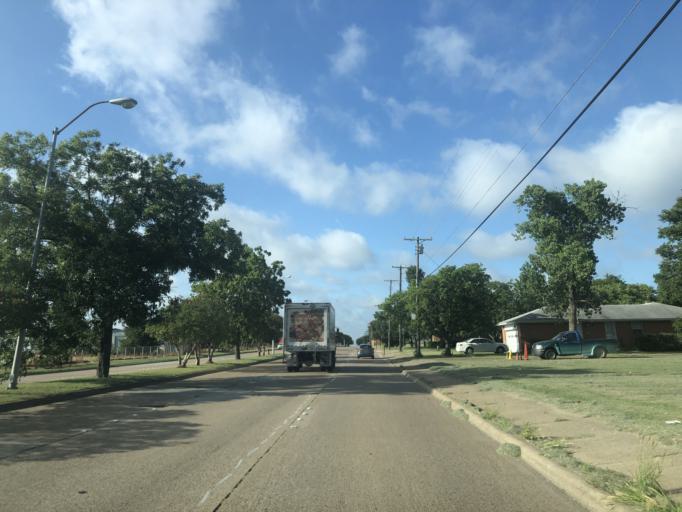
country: US
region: Texas
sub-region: Dallas County
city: Duncanville
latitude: 32.6728
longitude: -96.9087
